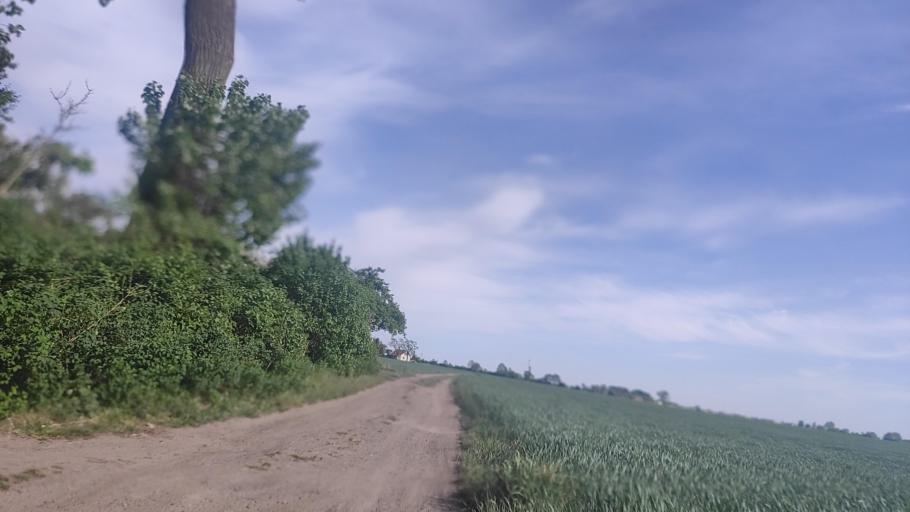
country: PL
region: Greater Poland Voivodeship
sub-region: Powiat poznanski
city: Swarzedz
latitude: 52.4175
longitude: 17.1468
